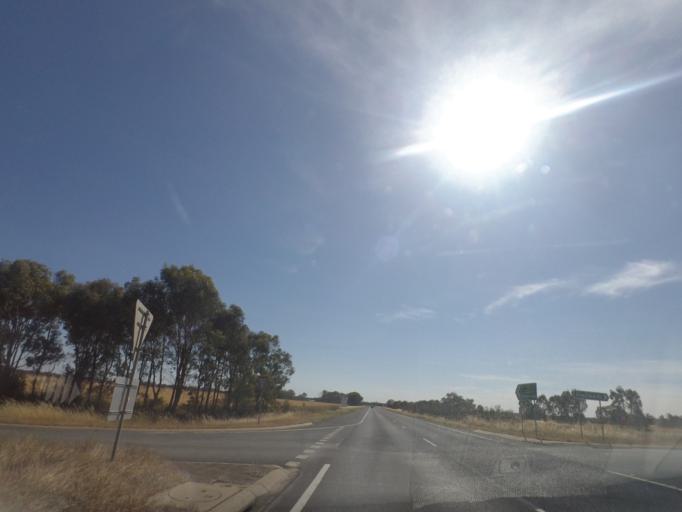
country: AU
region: Victoria
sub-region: Greater Shepparton
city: Shepparton
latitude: -36.6734
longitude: 145.2577
